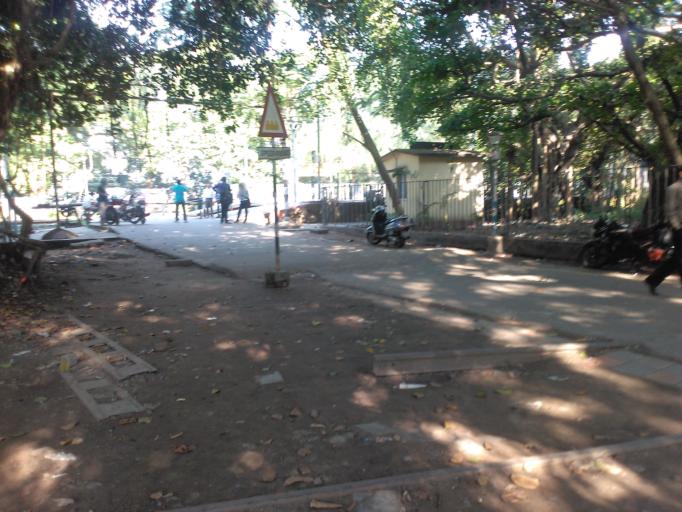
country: IN
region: West Bengal
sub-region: Kolkata
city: Bara Bazar
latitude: 22.5556
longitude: 88.3310
